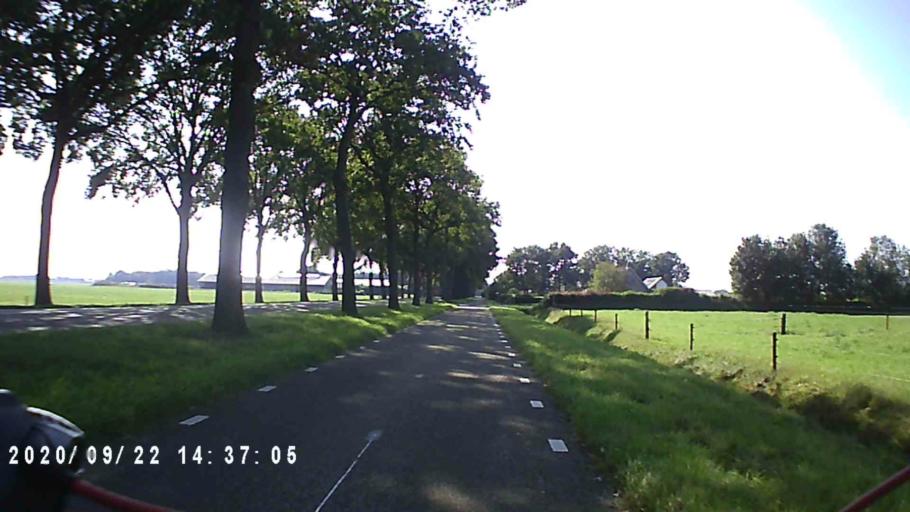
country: NL
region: Groningen
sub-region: Gemeente Leek
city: Leek
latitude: 53.0309
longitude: 6.3597
